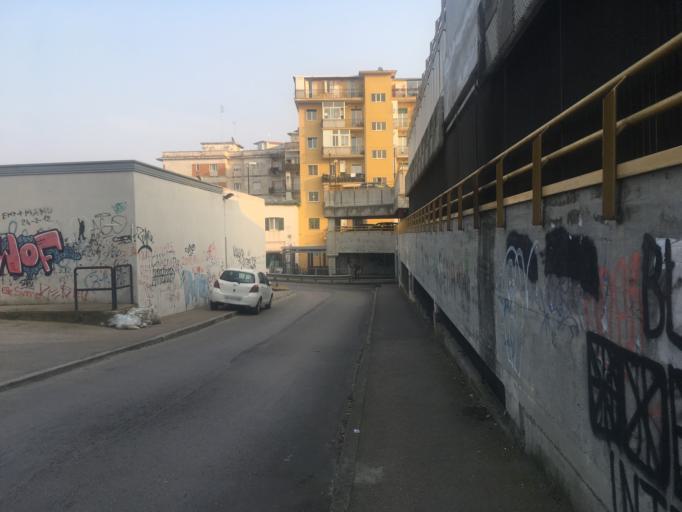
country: IT
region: Campania
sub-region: Provincia di Napoli
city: Napoli
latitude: 40.8695
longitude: 14.2278
